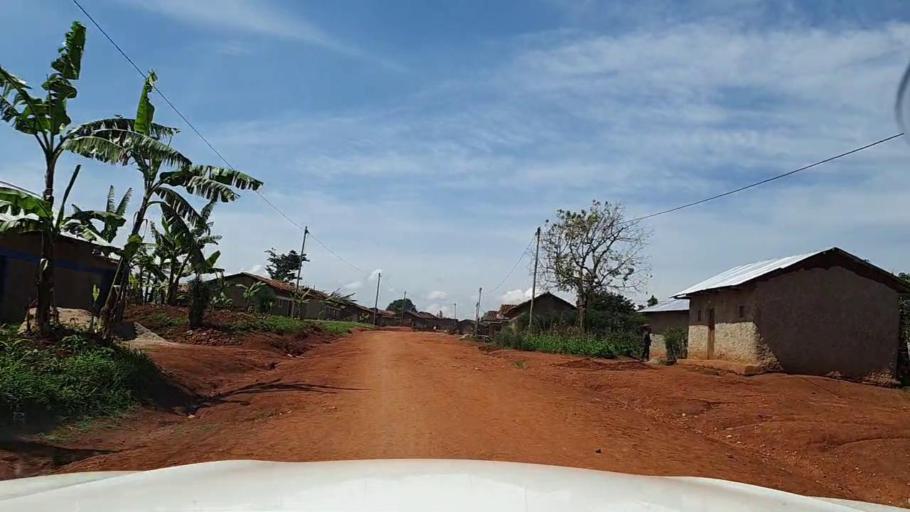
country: RW
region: Southern Province
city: Butare
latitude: -2.7195
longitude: 29.8379
